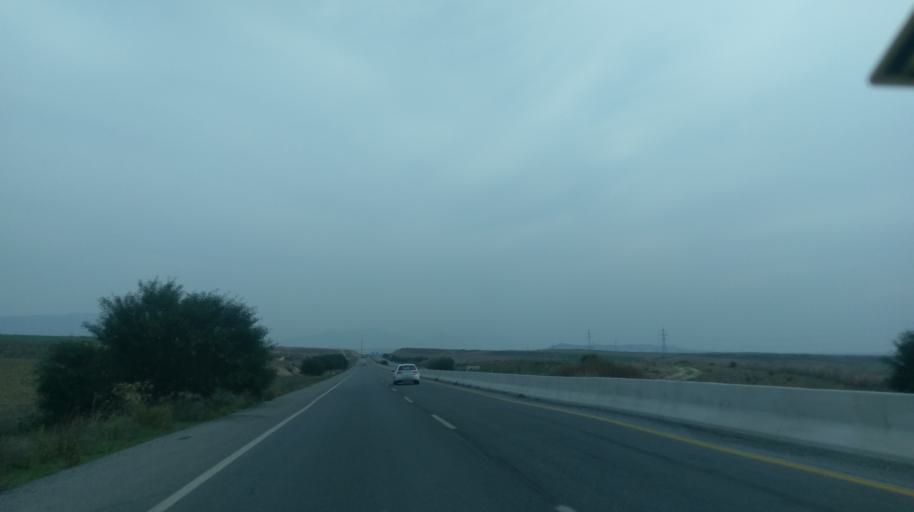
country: CY
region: Lefkosia
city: Mammari
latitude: 35.2183
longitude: 33.1414
